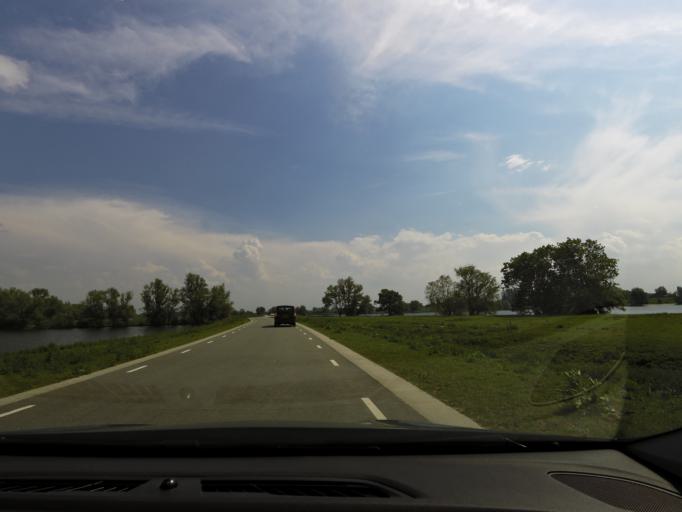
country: NL
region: North Brabant
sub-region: Gemeente Woudrichem
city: Woudrichem
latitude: 51.8073
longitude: 5.0240
